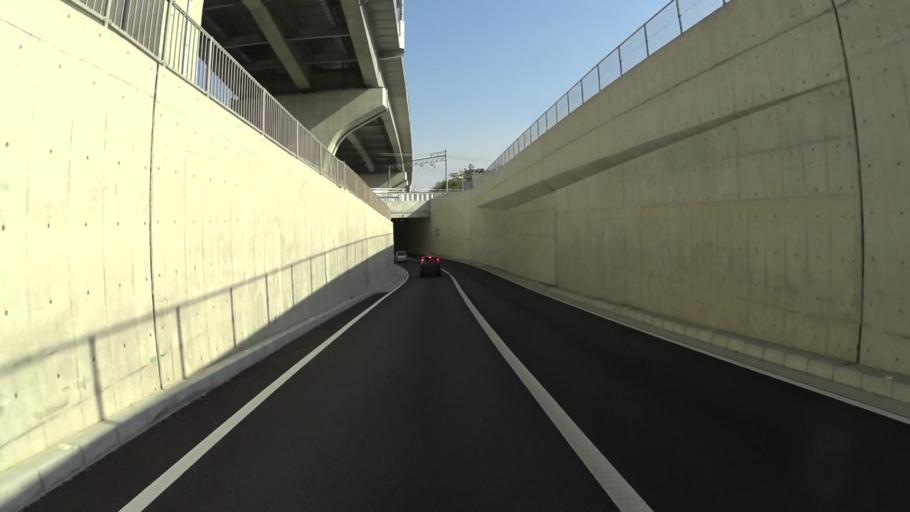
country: JP
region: Kyoto
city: Yawata
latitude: 34.9099
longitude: 135.6907
